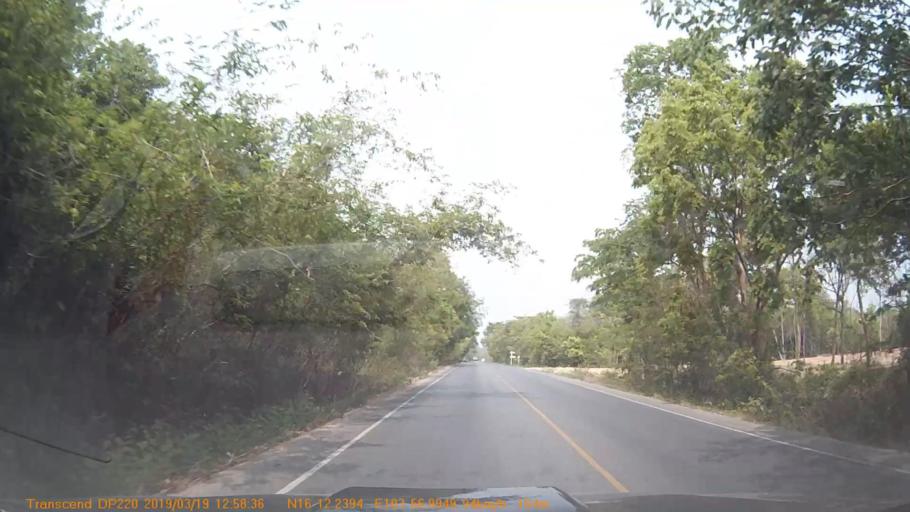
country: TH
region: Roi Et
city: Waeng
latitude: 16.2044
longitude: 103.9500
